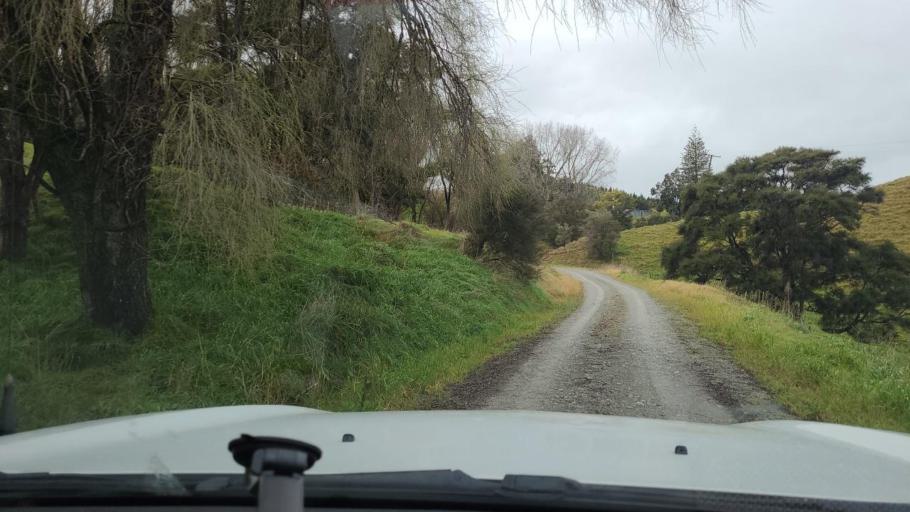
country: NZ
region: Gisborne
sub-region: Gisborne District
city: Gisborne
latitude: -38.5656
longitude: 177.7920
